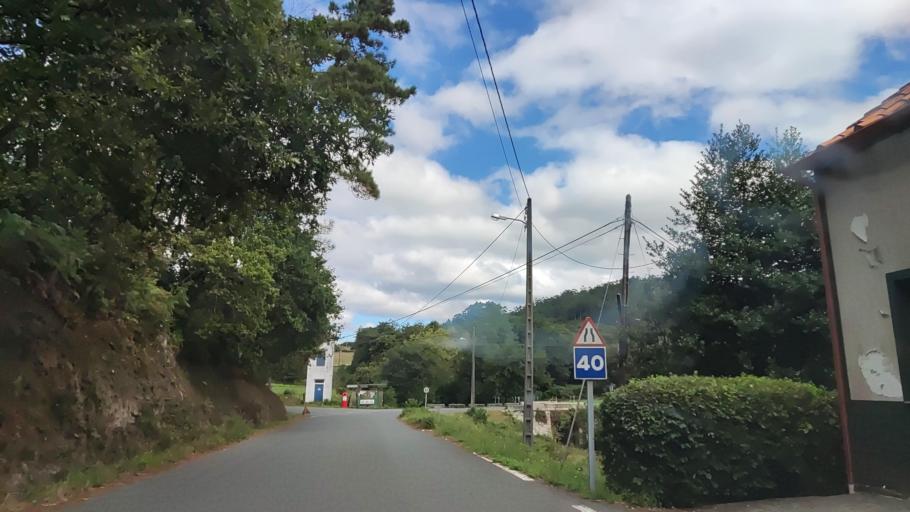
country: ES
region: Galicia
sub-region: Provincia da Coruna
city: Rois
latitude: 42.7409
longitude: -8.7004
